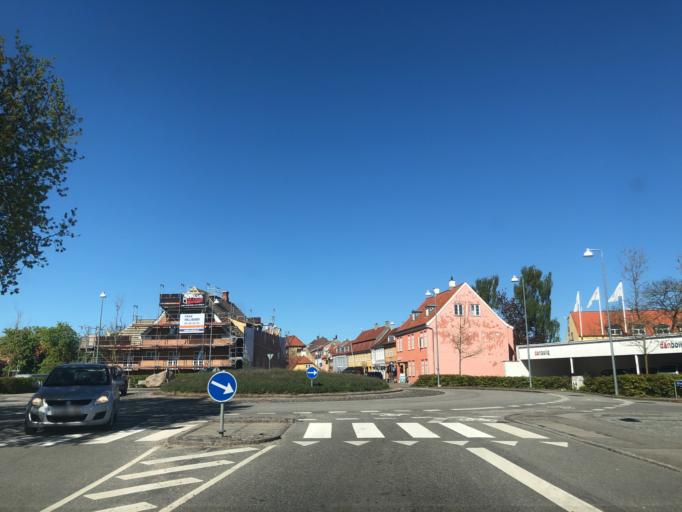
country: DK
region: Zealand
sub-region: Koge Kommune
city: Koge
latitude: 55.4539
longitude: 12.1806
